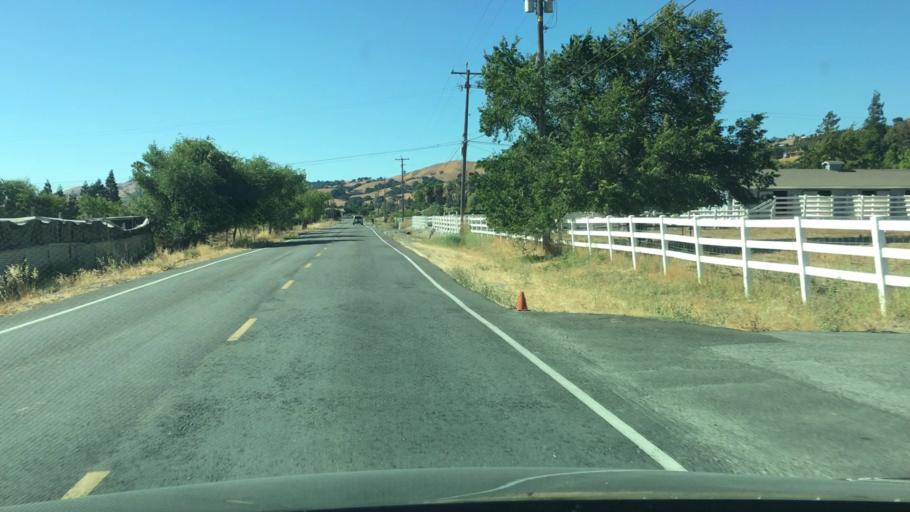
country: US
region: California
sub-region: Santa Clara County
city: San Martin
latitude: 37.1255
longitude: -121.5987
